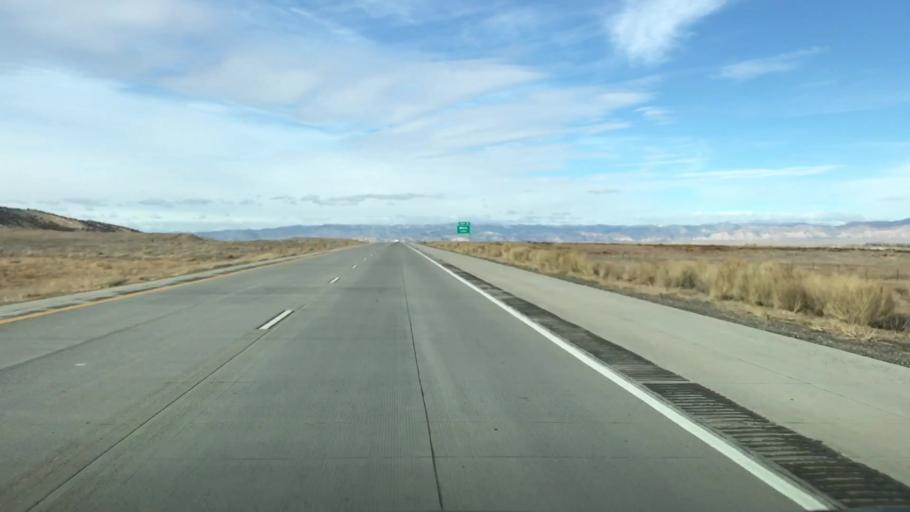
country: US
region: Colorado
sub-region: Mesa County
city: Loma
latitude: 39.2010
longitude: -108.8510
